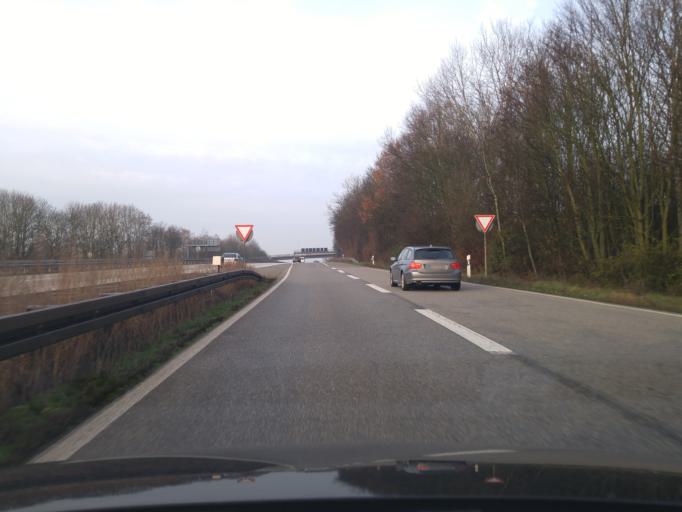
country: DE
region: Hesse
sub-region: Regierungsbezirk Giessen
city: Limburg an der Lahn
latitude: 50.4010
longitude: 8.0672
